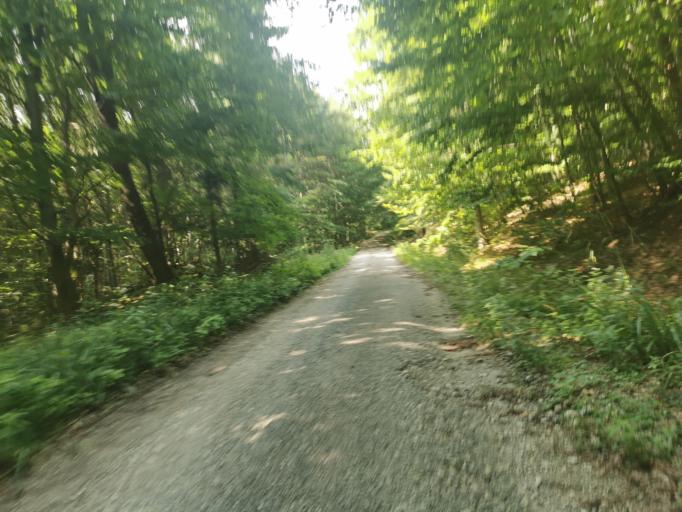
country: SK
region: Trenciansky
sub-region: Okres Myjava
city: Myjava
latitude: 48.8189
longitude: 17.5624
